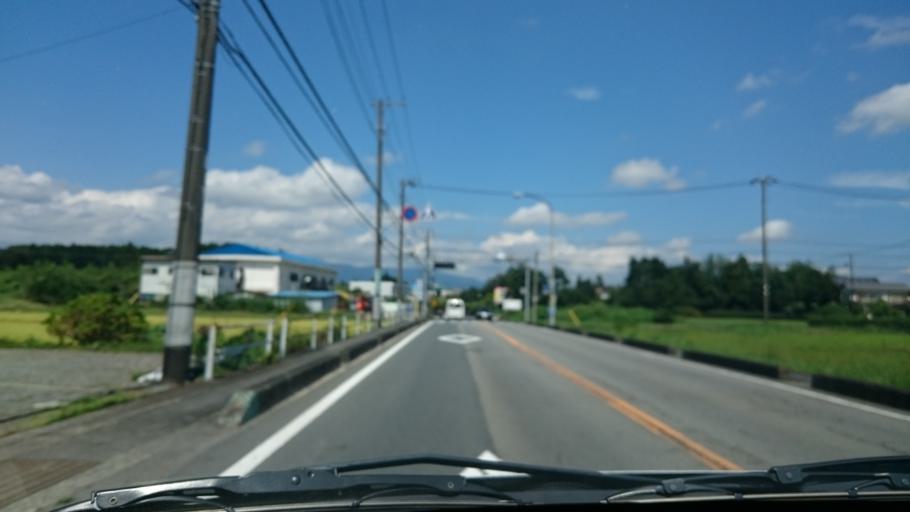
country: JP
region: Shizuoka
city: Gotemba
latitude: 35.2703
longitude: 138.9244
